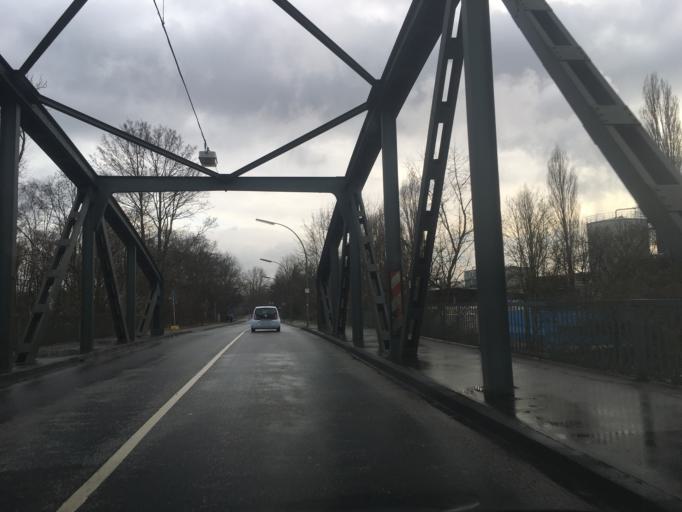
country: DE
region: North Rhine-Westphalia
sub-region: Regierungsbezirk Munster
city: Gelsenkirchen
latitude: 51.5433
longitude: 7.0838
